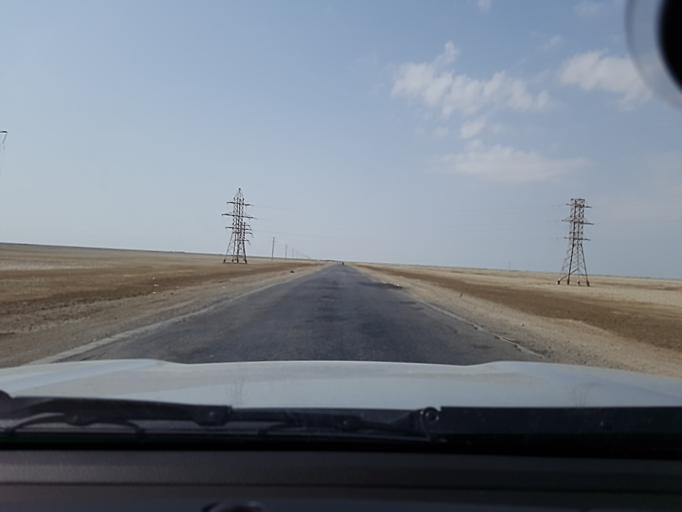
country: TM
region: Balkan
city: Gumdag
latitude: 39.0550
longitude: 54.5842
